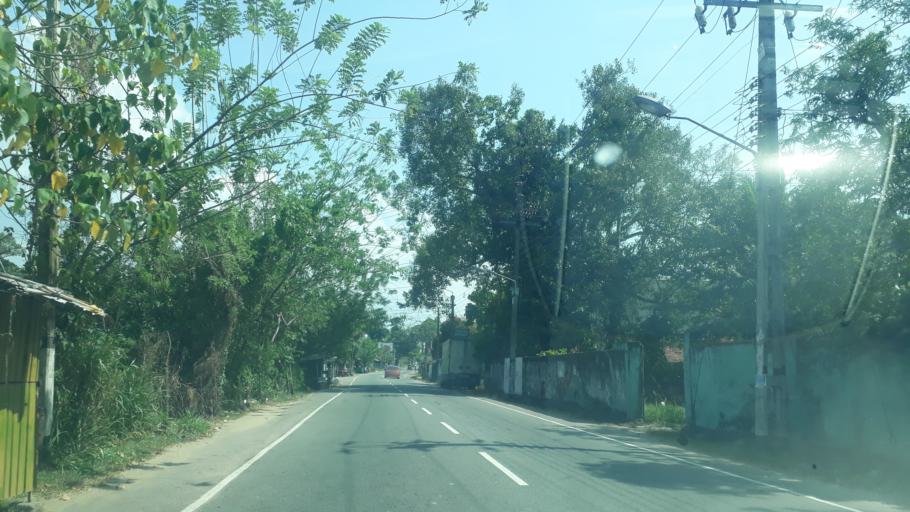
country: LK
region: Western
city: Gampaha
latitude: 7.0828
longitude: 80.0107
